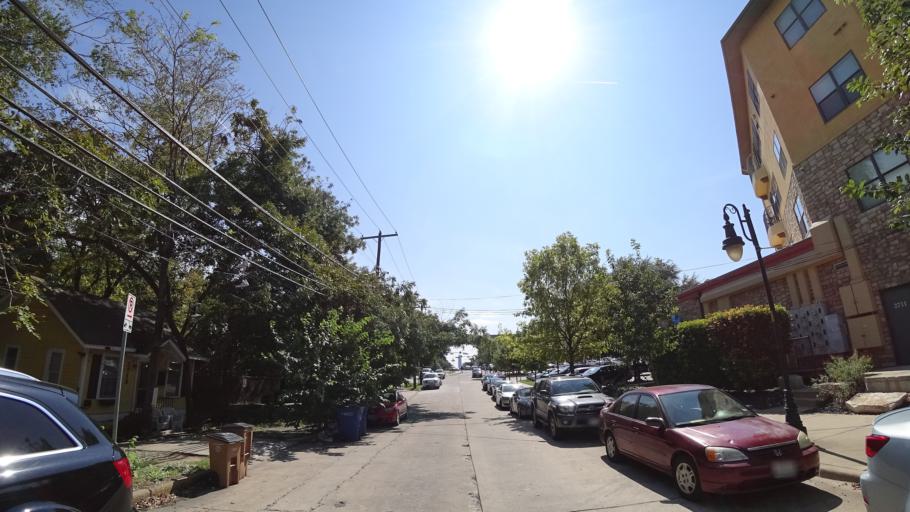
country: US
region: Texas
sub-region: Travis County
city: Austin
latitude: 30.2931
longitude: -97.7411
